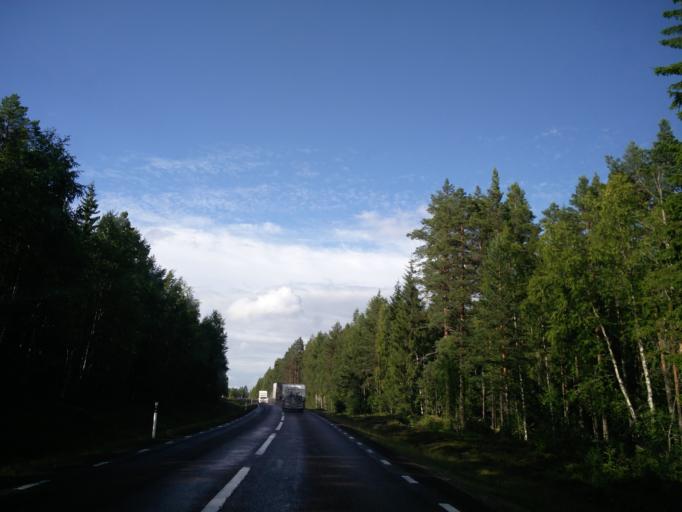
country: SE
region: Vaermland
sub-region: Hagfors Kommun
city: Ekshaerad
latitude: 60.4912
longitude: 13.4134
